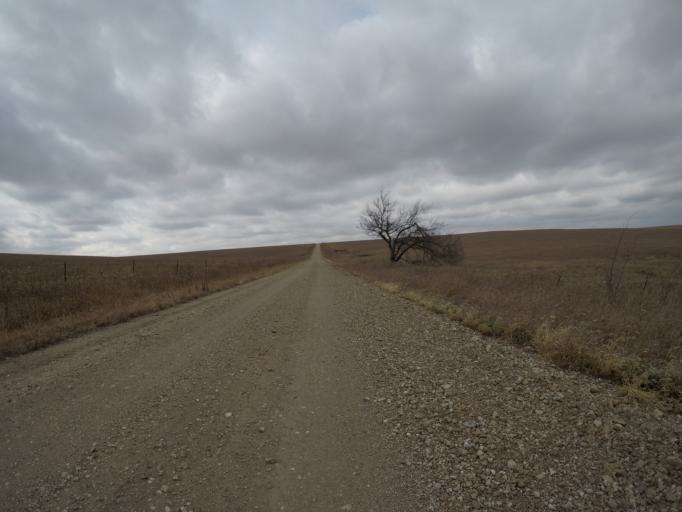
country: US
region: Kansas
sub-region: Morris County
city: Council Grove
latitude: 38.7244
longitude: -96.2013
